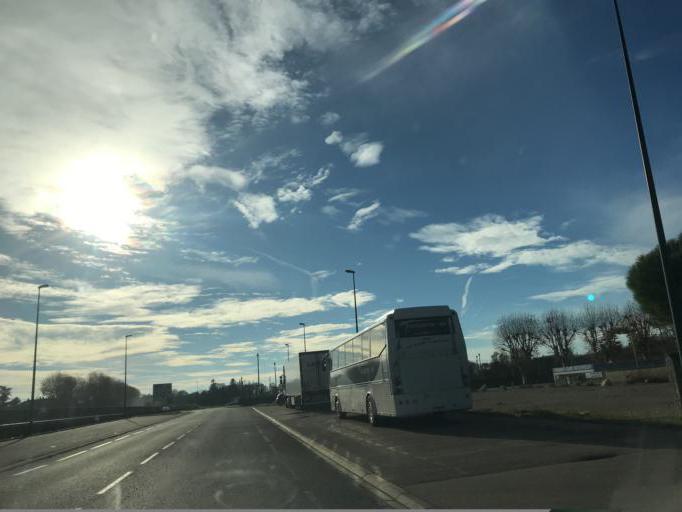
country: FR
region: Rhone-Alpes
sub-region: Departement de l'Ain
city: Meximieux
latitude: 45.8998
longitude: 5.1950
